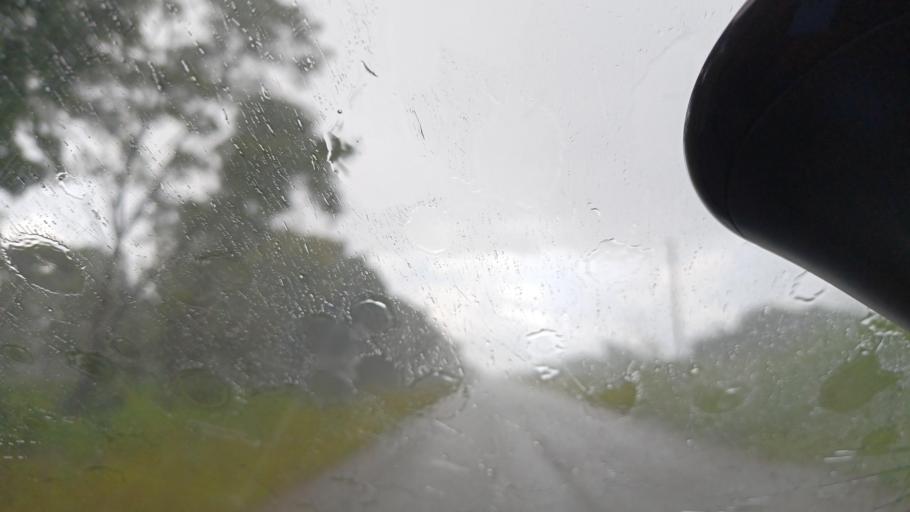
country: ZM
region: North-Western
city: Kasempa
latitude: -13.0941
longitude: 25.9179
